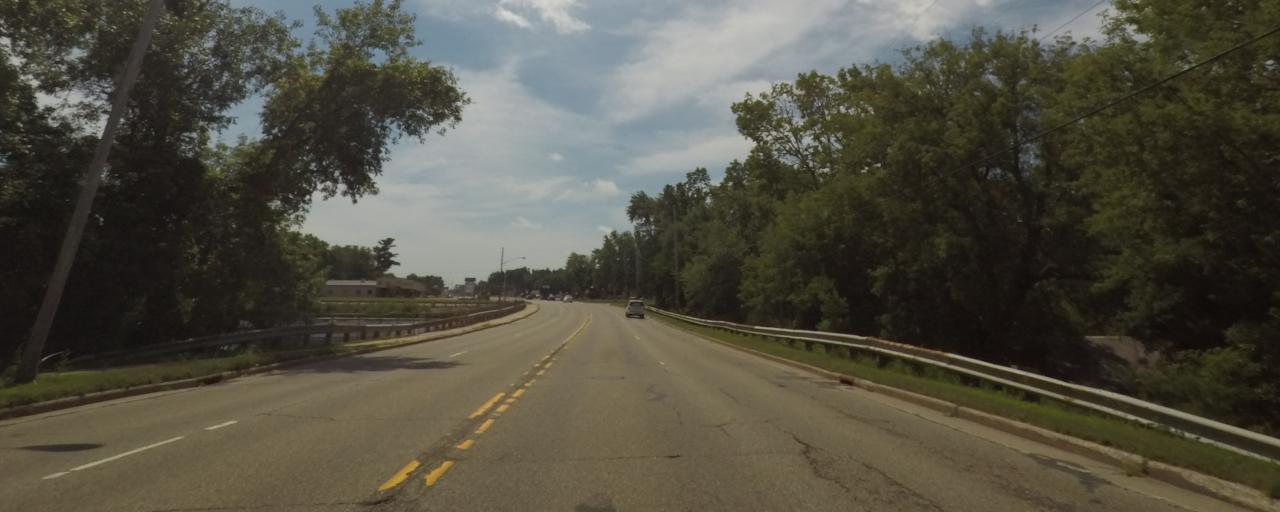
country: US
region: Wisconsin
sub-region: Portage County
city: Plover
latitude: 44.4727
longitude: -89.5476
